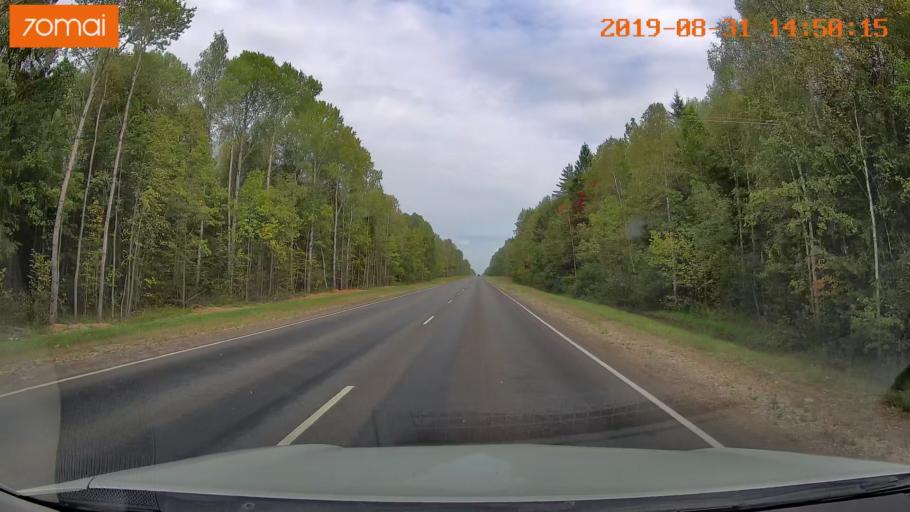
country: RU
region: Kaluga
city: Spas-Demensk
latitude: 54.2600
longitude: 33.7852
